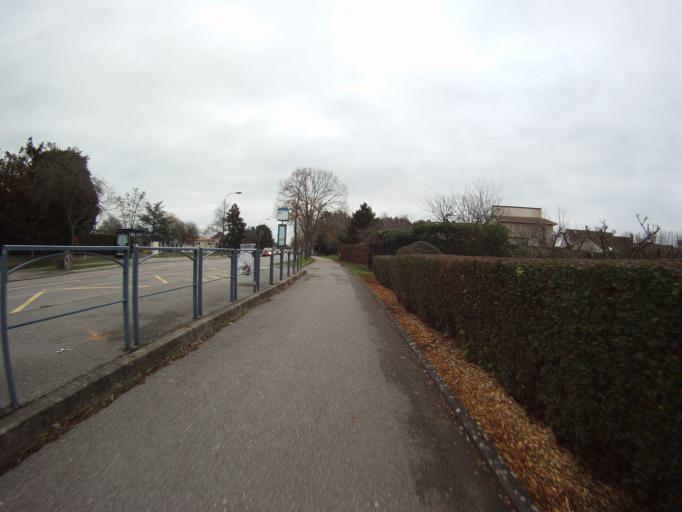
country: FR
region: Lorraine
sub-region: Departement de Meurthe-et-Moselle
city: Pulnoy
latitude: 48.7043
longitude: 6.2542
